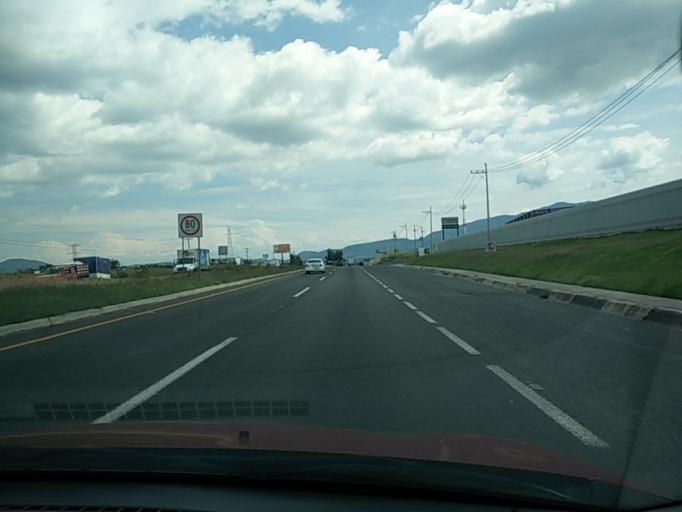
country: MX
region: Jalisco
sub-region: Ixtlahuacan de los Membrillos
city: Los Olivos
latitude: 20.4333
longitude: -103.2415
